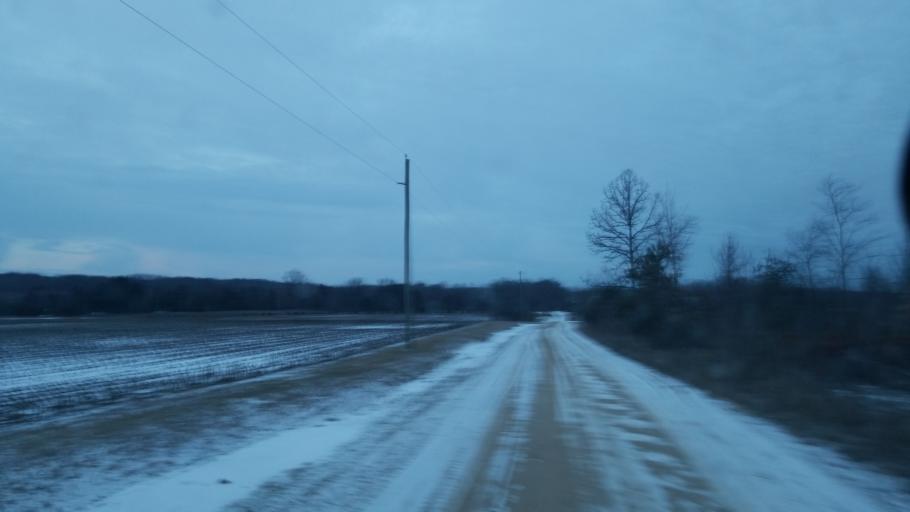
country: US
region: Michigan
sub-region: Osceola County
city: Reed City
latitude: 43.8292
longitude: -85.4258
